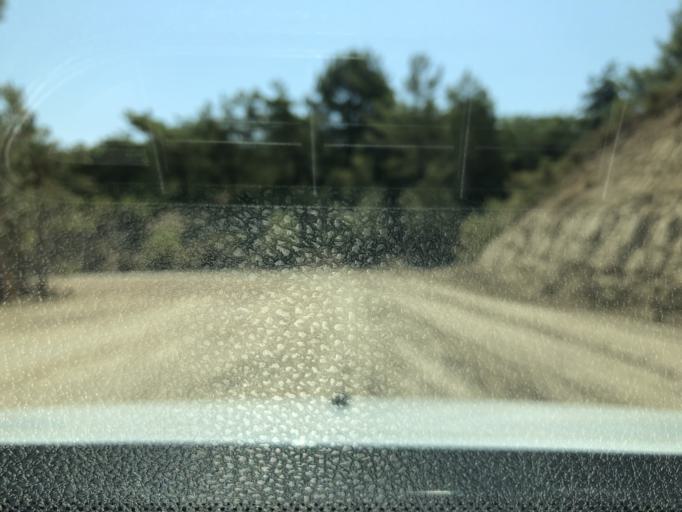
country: TR
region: Antalya
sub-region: Manavgat
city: Manavgat
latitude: 36.8258
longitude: 31.5083
